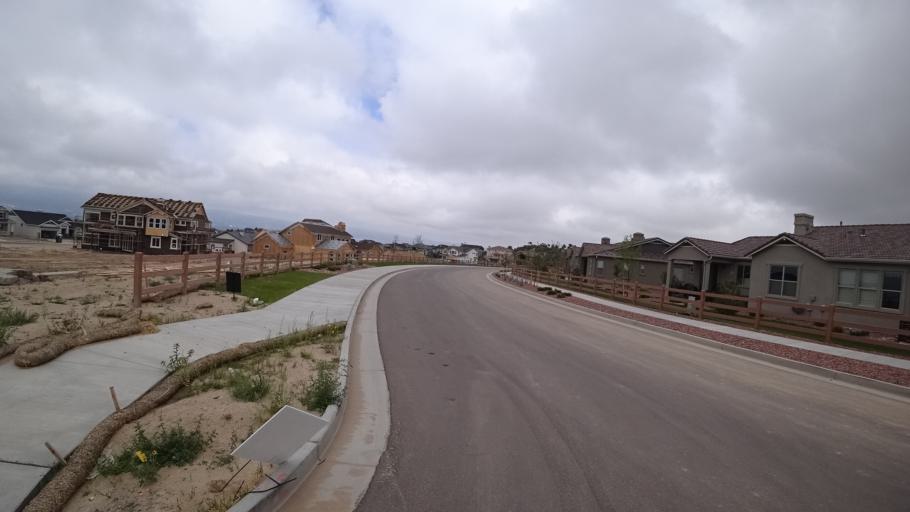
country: US
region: Colorado
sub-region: El Paso County
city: Gleneagle
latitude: 39.0070
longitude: -104.7864
